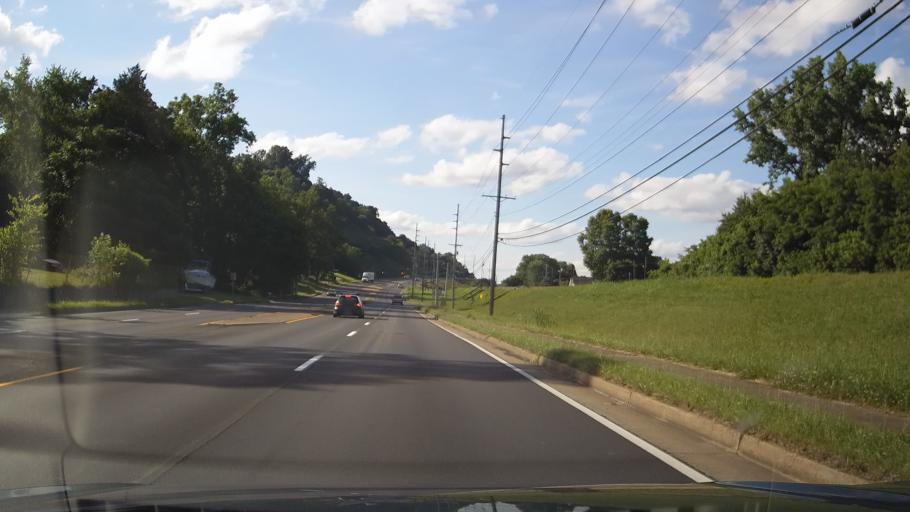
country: US
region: Kentucky
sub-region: Boyd County
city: Catlettsburg
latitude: 38.4184
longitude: -82.6002
